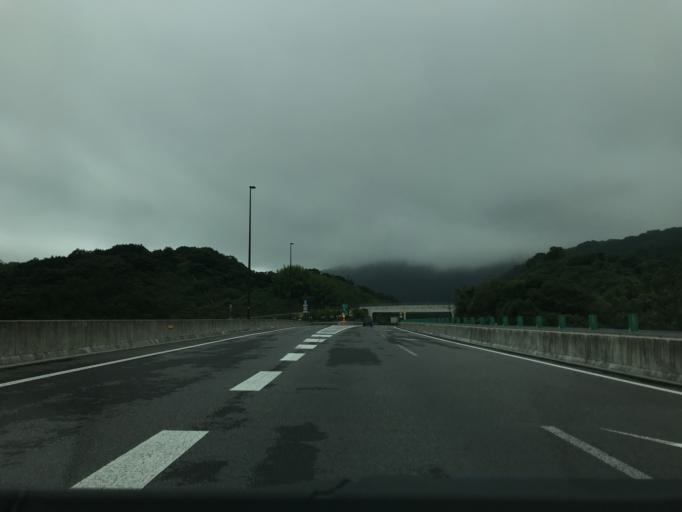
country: JP
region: Oita
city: Bungo-Takada-shi
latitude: 33.4997
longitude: 131.3162
